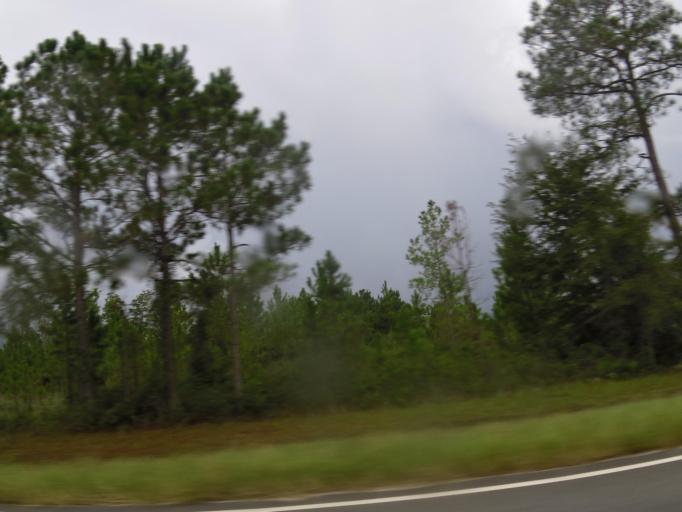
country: US
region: Florida
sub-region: Baker County
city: Macclenny
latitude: 30.4136
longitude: -82.1957
